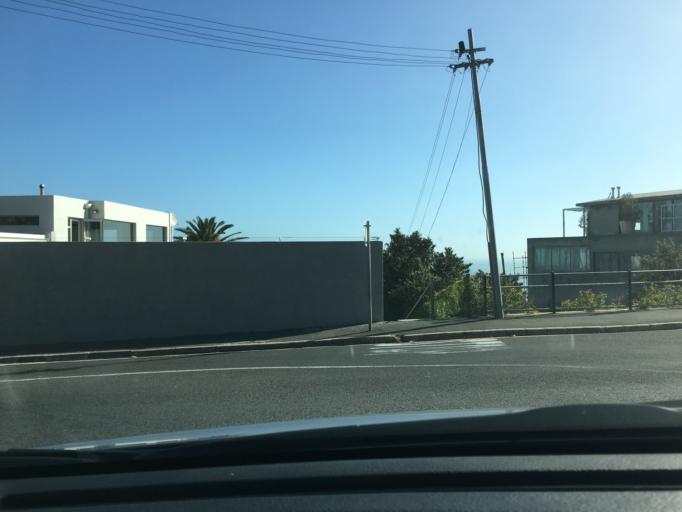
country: ZA
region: Western Cape
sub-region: City of Cape Town
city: Cape Town
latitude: -33.9614
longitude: 18.3750
